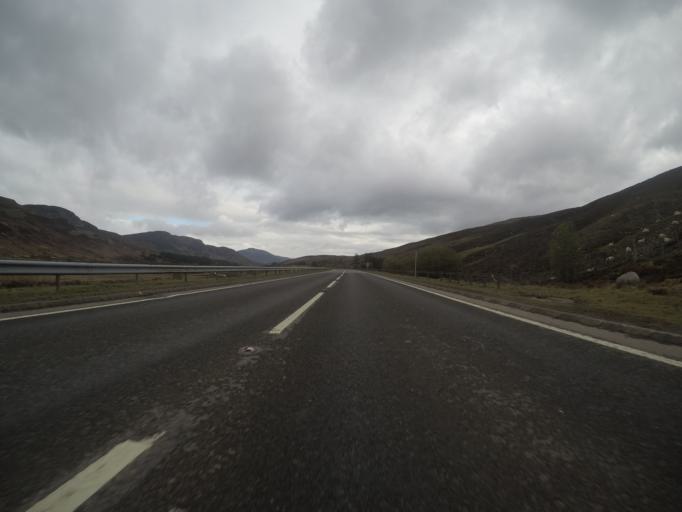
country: GB
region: Scotland
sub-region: Highland
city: Kingussie
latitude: 56.9790
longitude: -4.1797
